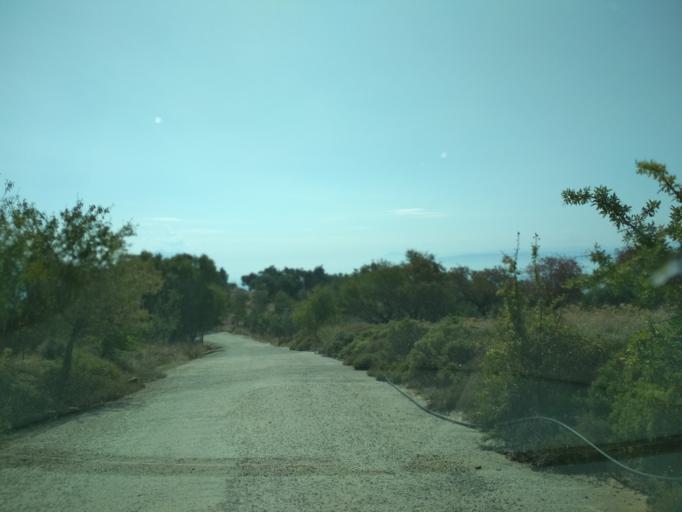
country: GR
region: Central Greece
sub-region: Nomos Evvoias
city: Oreoi
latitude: 38.8521
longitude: 23.1114
